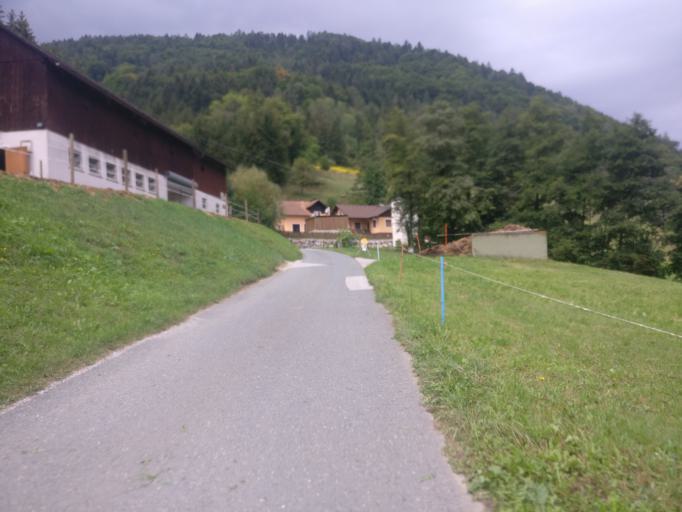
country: AT
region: Styria
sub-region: Politischer Bezirk Graz-Umgebung
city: Frohnleiten
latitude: 47.2393
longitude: 15.3102
